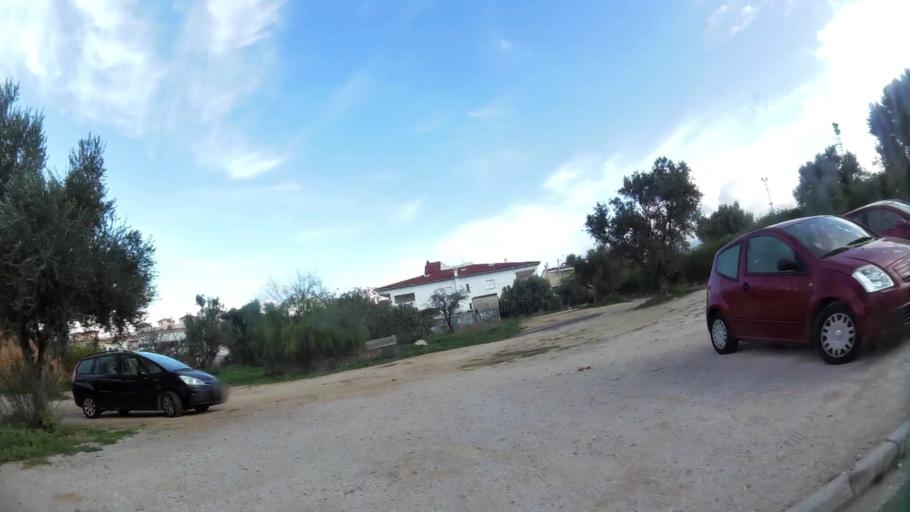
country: GR
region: Attica
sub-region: Nomarchia Athinas
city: Vrilissia
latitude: 38.0411
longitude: 23.8215
